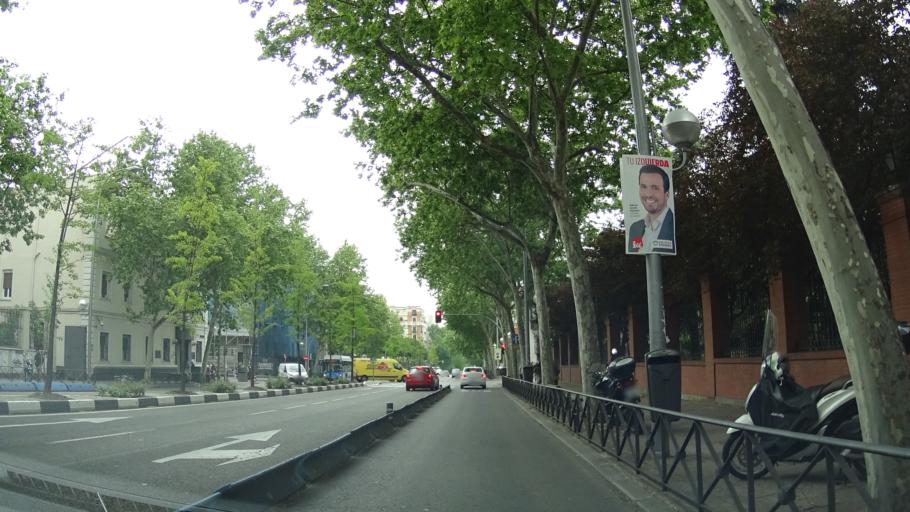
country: ES
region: Madrid
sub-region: Provincia de Madrid
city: Salamanca
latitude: 40.4320
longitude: -3.6797
